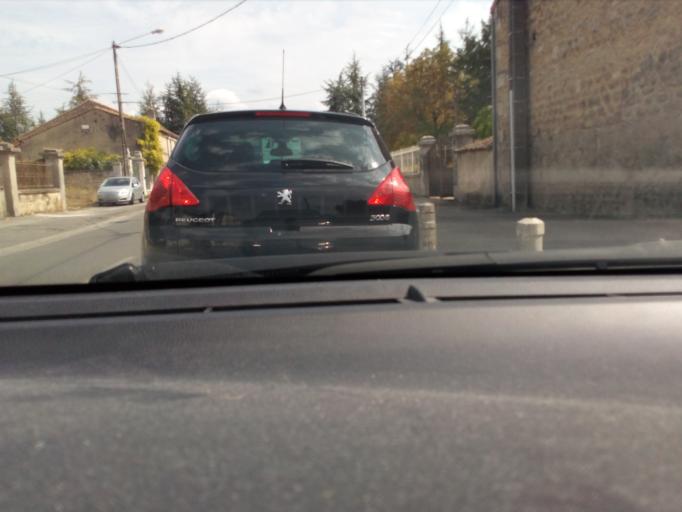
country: FR
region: Poitou-Charentes
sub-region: Departement de la Charente
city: Saint-Yrieix-sur-Charente
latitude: 45.6646
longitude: 0.1272
